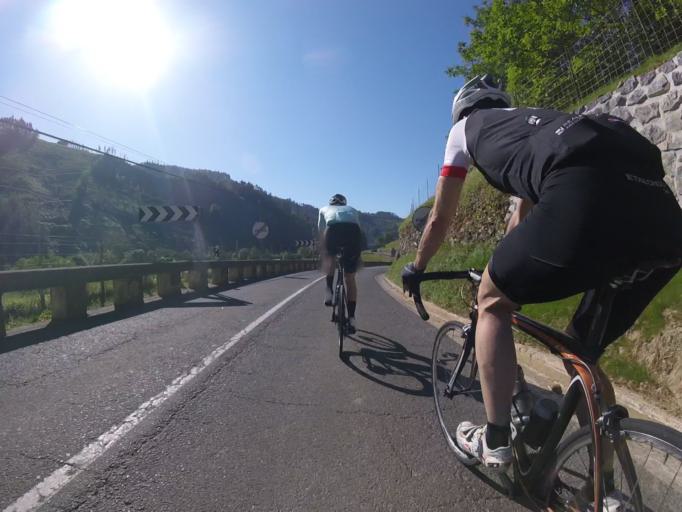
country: ES
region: Basque Country
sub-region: Provincia de Guipuzcoa
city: Azpeitia
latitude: 43.1532
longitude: -2.2411
